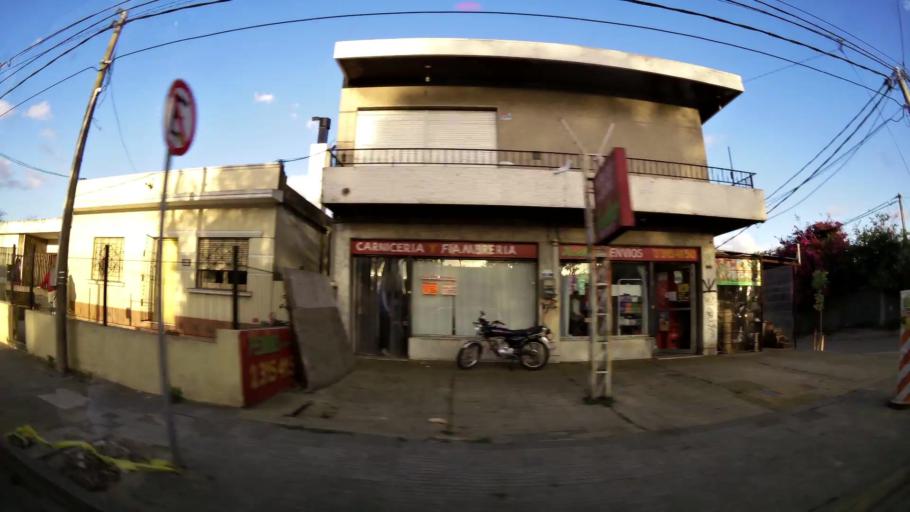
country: UY
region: Montevideo
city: Montevideo
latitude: -34.8820
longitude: -56.2497
